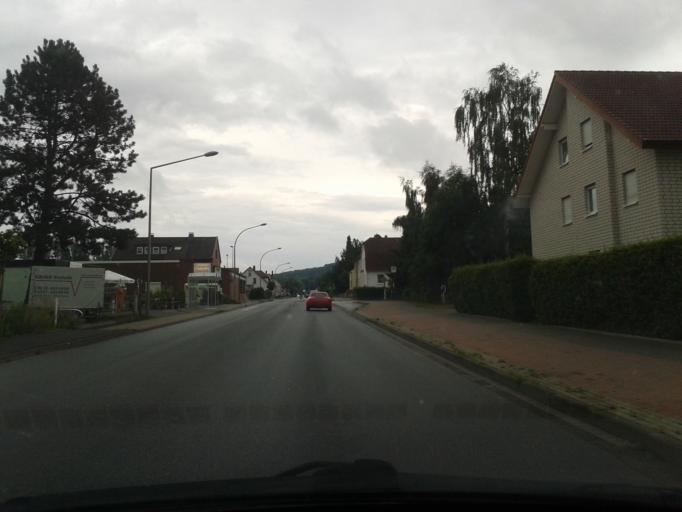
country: DE
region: North Rhine-Westphalia
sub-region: Regierungsbezirk Detmold
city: Detmold
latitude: 51.9196
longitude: 8.9014
